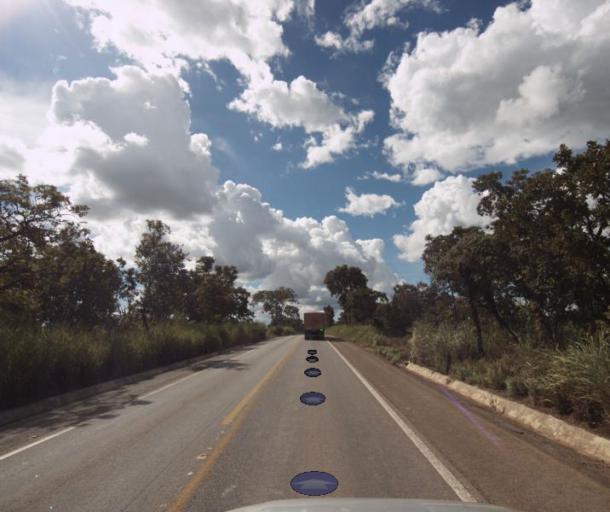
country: BR
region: Goias
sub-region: Porangatu
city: Porangatu
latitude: -13.2456
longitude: -49.1402
